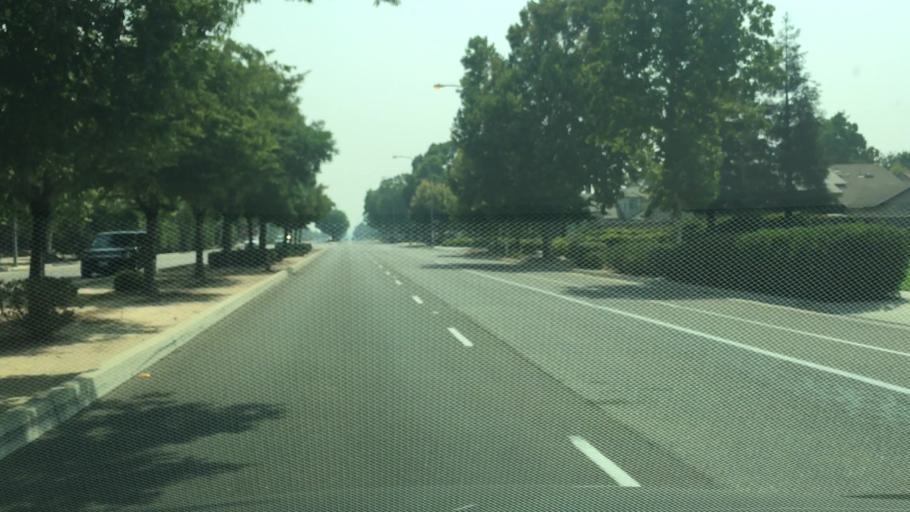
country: US
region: California
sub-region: Fresno County
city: Clovis
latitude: 36.8665
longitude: -119.7460
